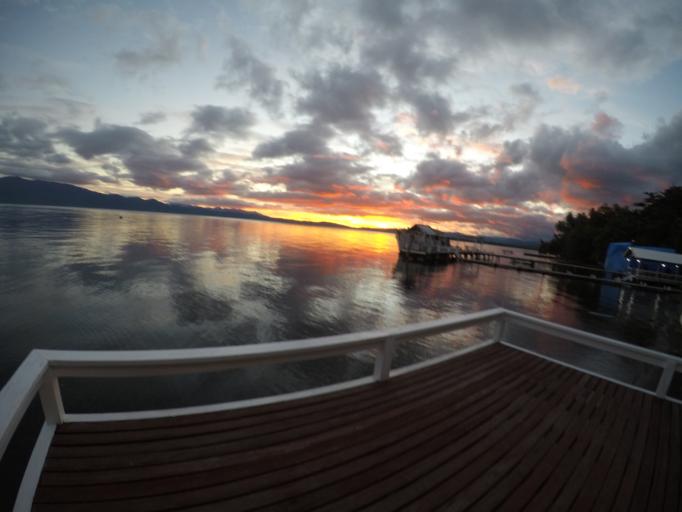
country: PG
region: Milne Bay
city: Alotau
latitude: -10.3112
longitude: 150.4232
